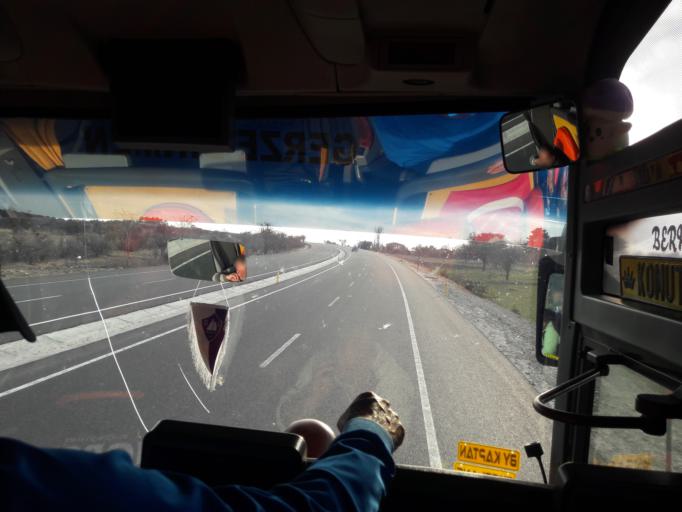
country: TR
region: Cankiri
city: Ilgaz
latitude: 40.8581
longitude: 33.6156
